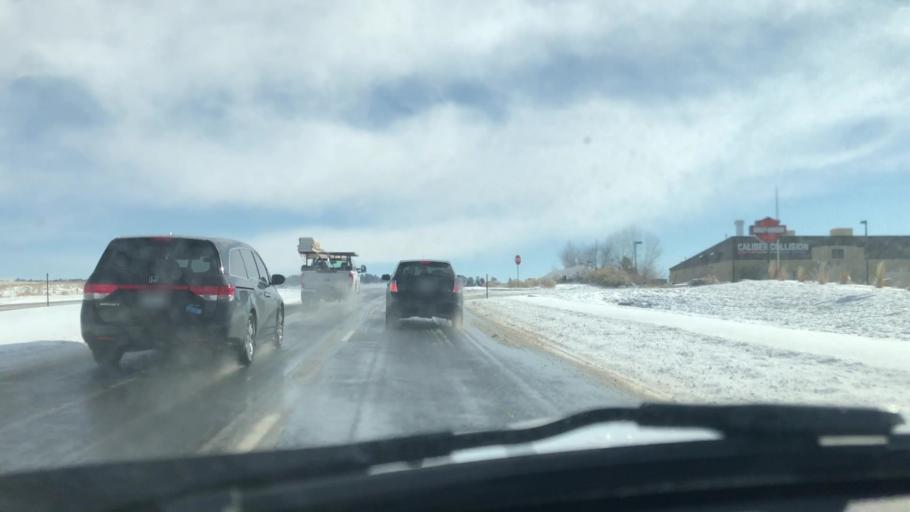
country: US
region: Colorado
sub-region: Douglas County
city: Parker
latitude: 39.5441
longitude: -104.7703
